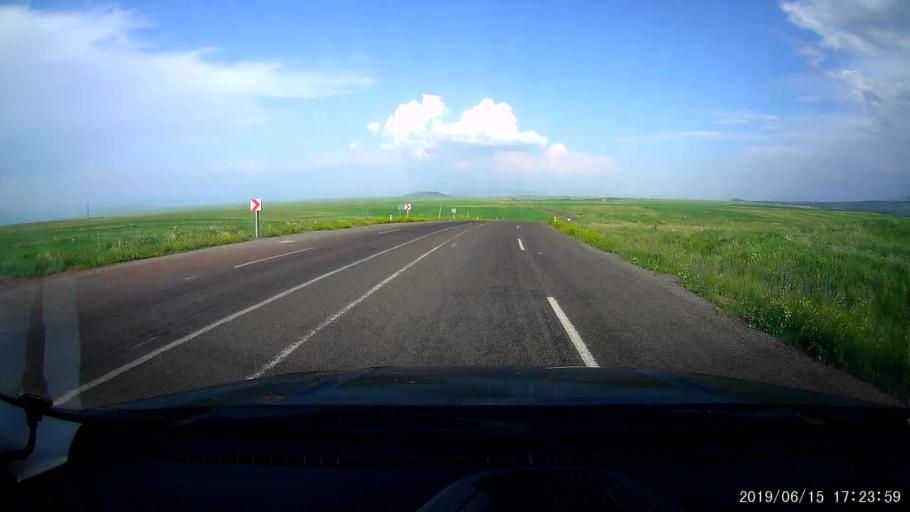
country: TR
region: Kars
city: Basgedikler
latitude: 40.6162
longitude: 43.3744
